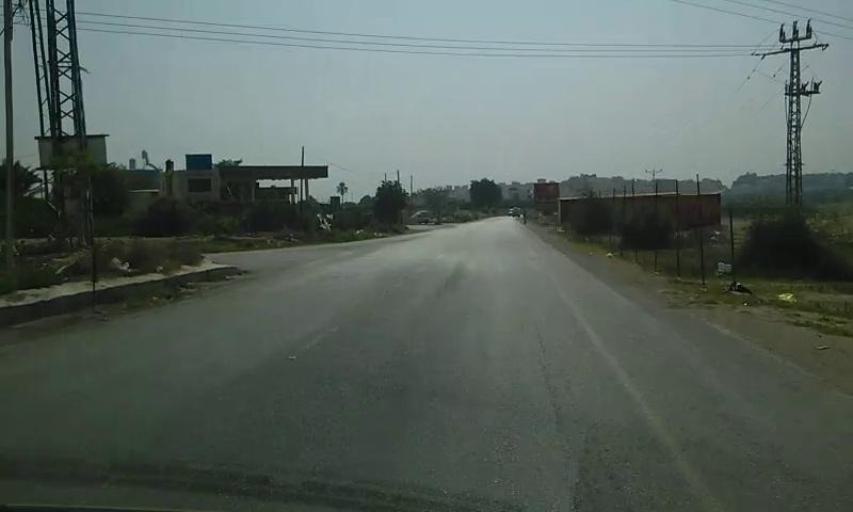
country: PS
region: West Bank
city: An Nuway`imah
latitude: 31.8881
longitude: 35.4341
